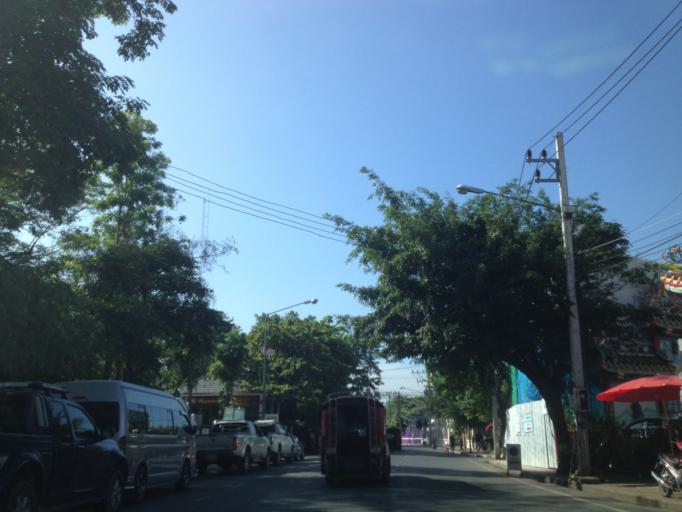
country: TH
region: Chiang Mai
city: Chiang Mai
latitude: 18.7901
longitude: 99.0023
